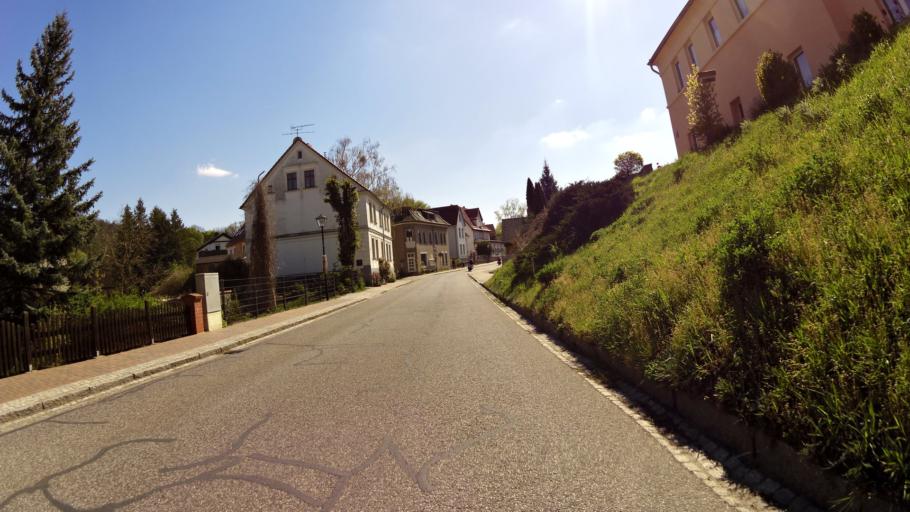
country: DE
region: Brandenburg
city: Buckow
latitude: 52.5636
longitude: 14.0749
